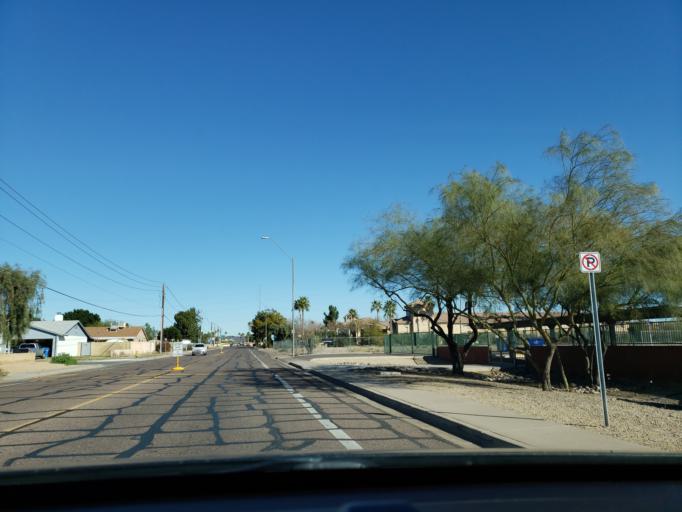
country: US
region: Arizona
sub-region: Maricopa County
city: Glendale
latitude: 33.6513
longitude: -112.1171
